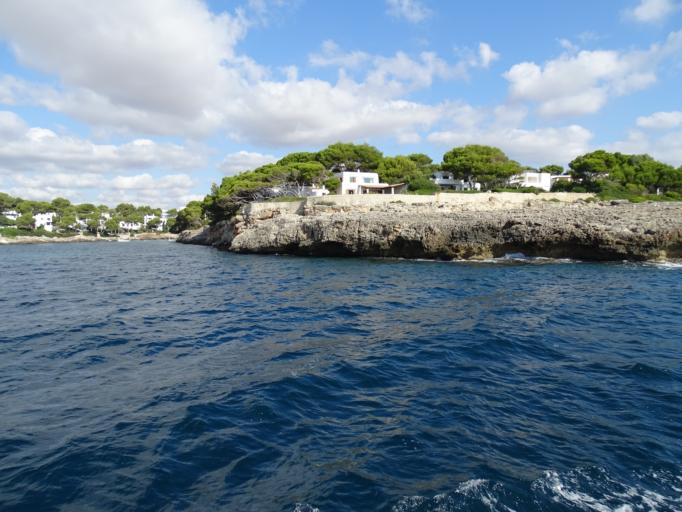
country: ES
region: Balearic Islands
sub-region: Illes Balears
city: Santanyi
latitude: 39.3688
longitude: 3.2336
